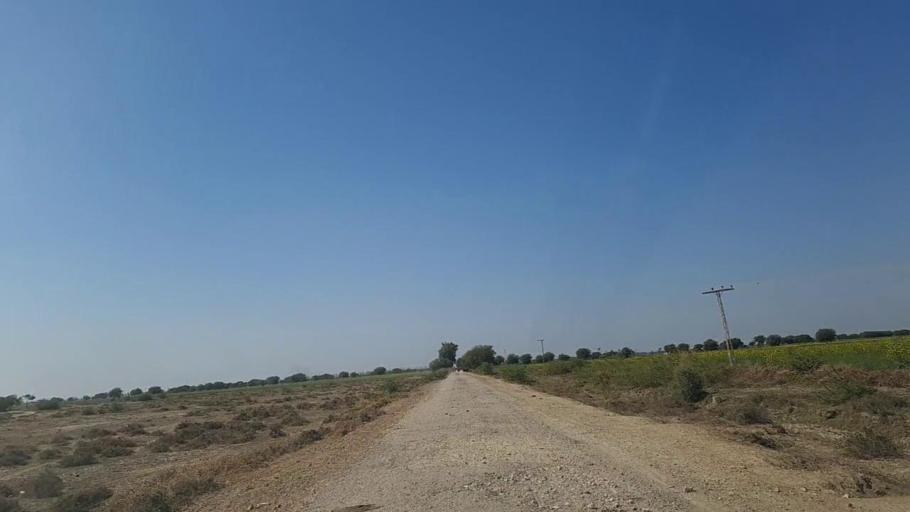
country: PK
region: Sindh
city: Naukot
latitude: 25.0380
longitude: 69.3865
